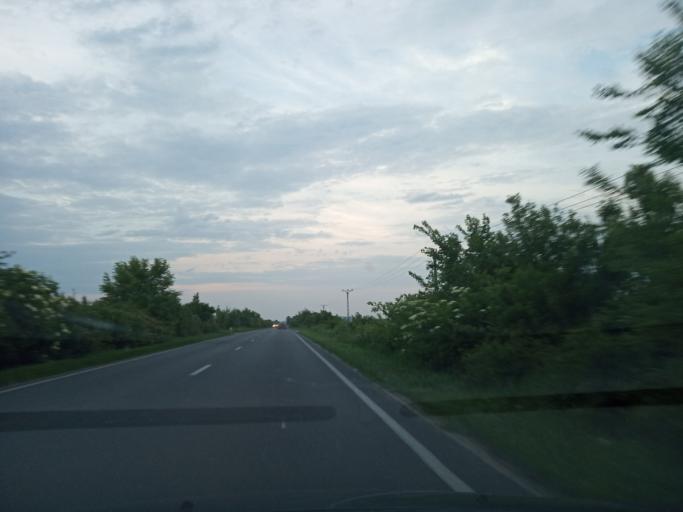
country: RO
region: Timis
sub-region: Oras Deta
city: Deta
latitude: 45.4263
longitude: 21.2302
